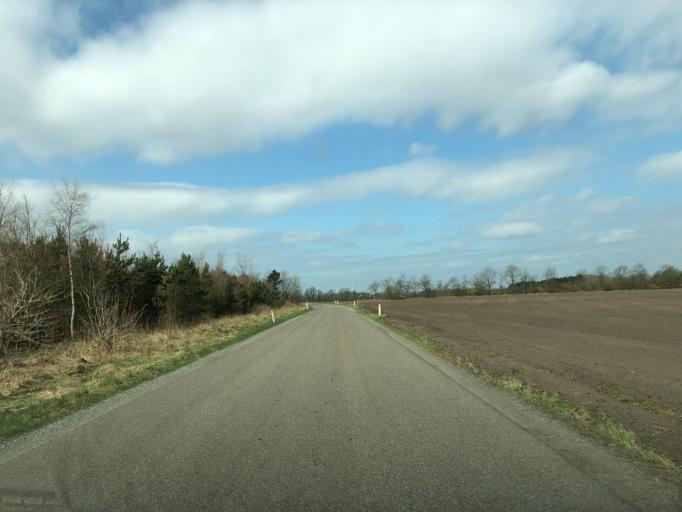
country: DK
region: South Denmark
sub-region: Vejle Kommune
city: Give
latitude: 55.9133
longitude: 9.2434
